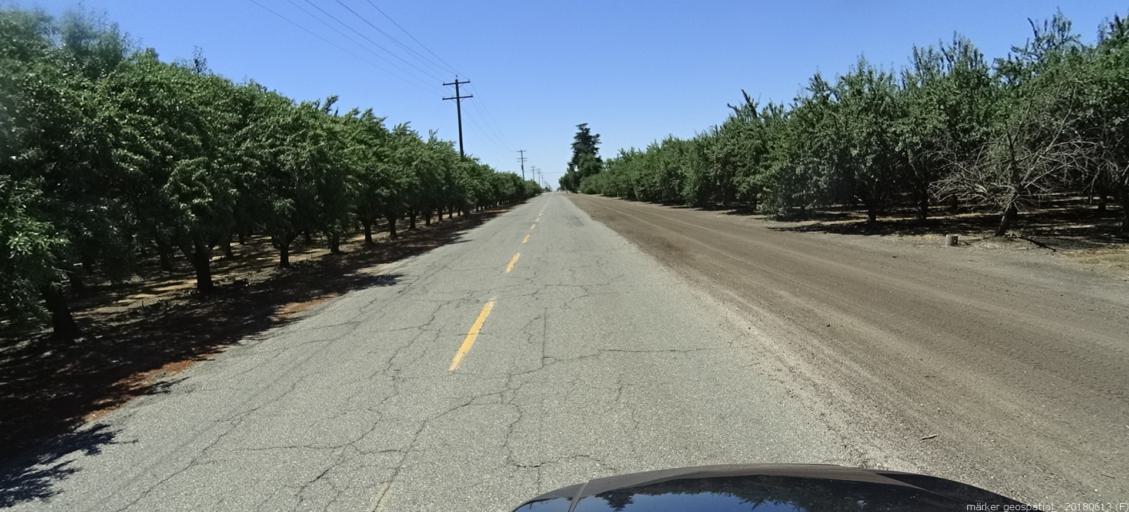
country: US
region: California
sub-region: Madera County
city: Chowchilla
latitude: 37.0286
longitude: -120.3106
